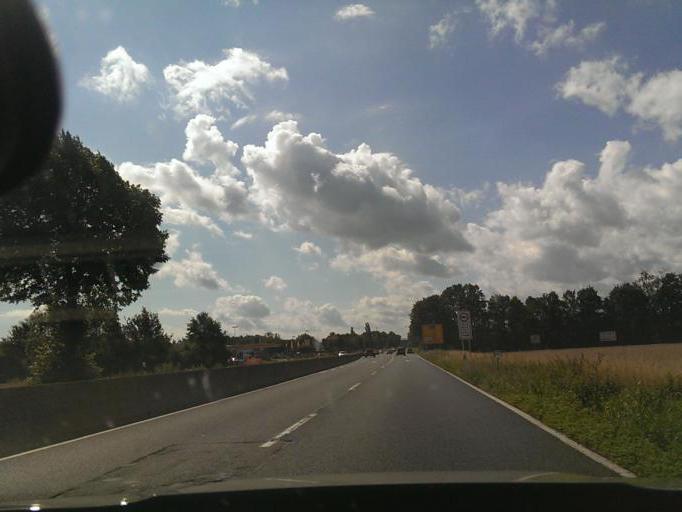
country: DE
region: Lower Saxony
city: Sarstedt
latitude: 52.2766
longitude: 9.8458
